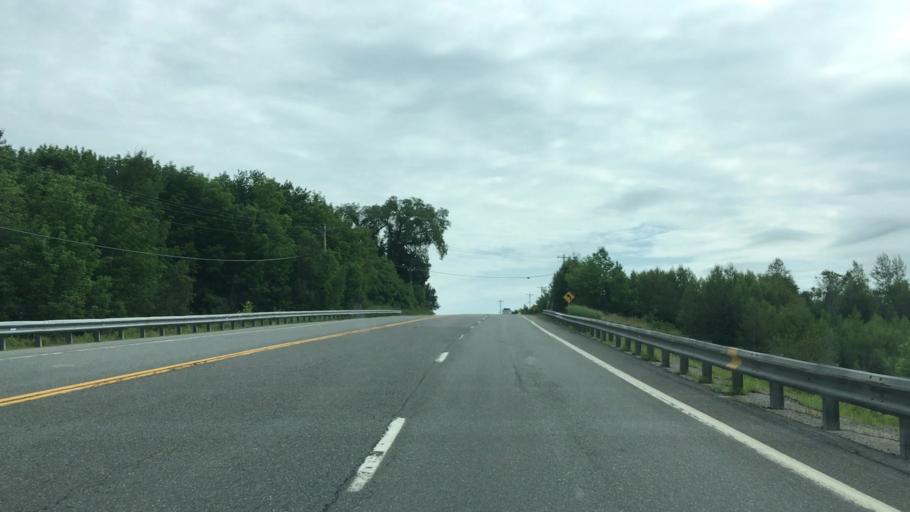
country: US
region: Maine
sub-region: Washington County
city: Calais
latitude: 45.0920
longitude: -67.4821
